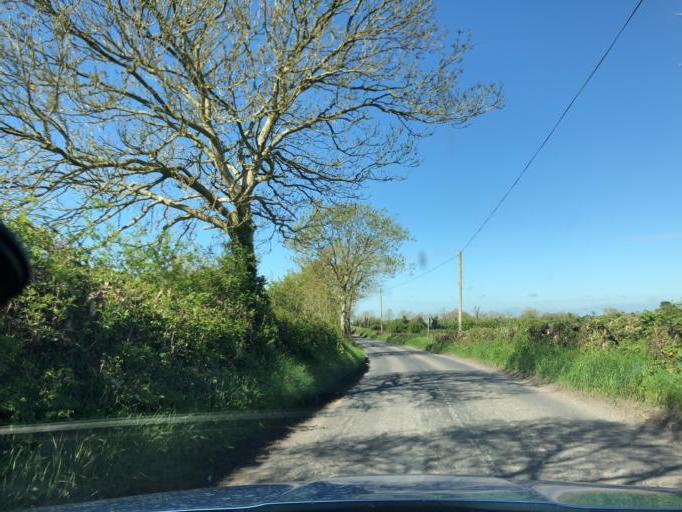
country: IE
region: Leinster
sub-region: Uibh Fhaili
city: Banagher
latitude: 53.2069
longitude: -8.0812
